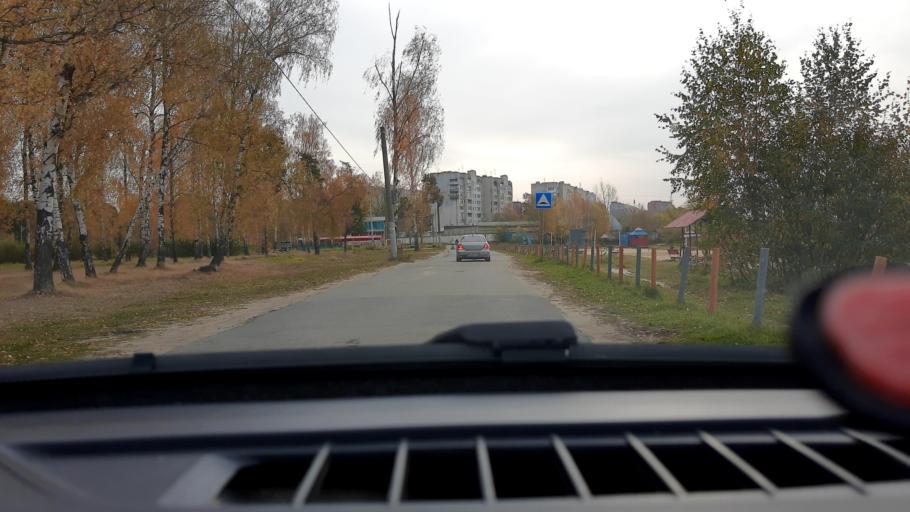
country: RU
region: Nizjnij Novgorod
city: Gorbatovka
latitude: 56.2935
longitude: 43.8358
